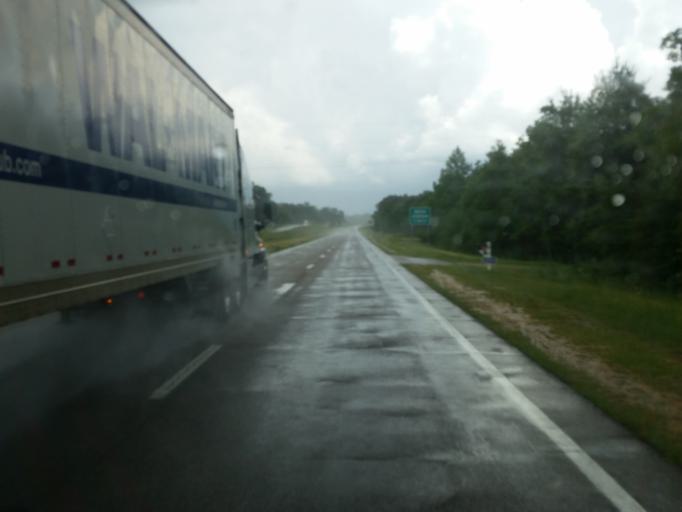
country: US
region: Mississippi
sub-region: George County
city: Lucedale
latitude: 30.9022
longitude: -88.4648
